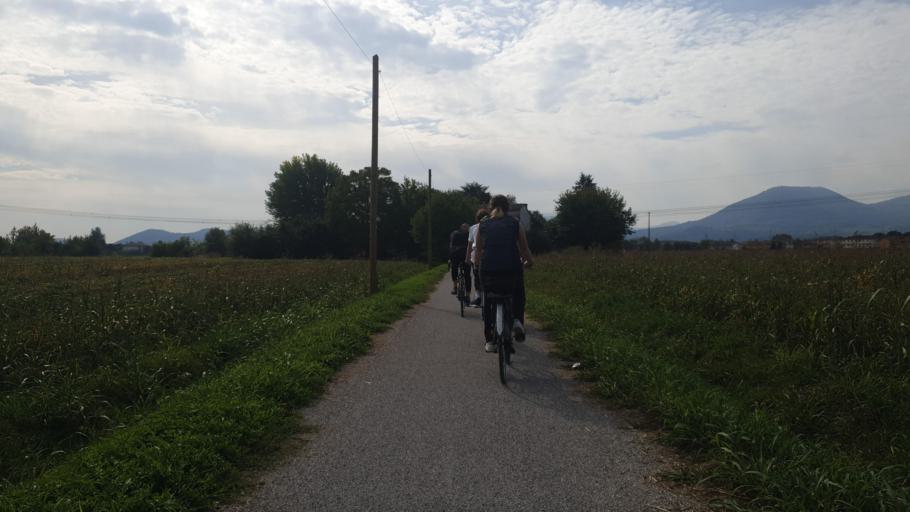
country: IT
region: Veneto
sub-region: Provincia di Padova
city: Cervarese Santa Croce
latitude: 45.4103
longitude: 11.6967
